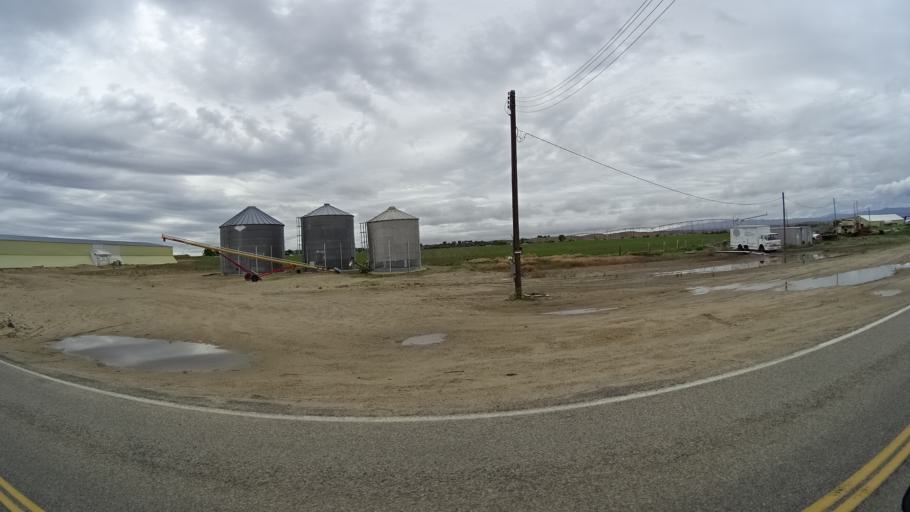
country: US
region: Idaho
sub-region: Ada County
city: Star
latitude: 43.7099
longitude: -116.4619
